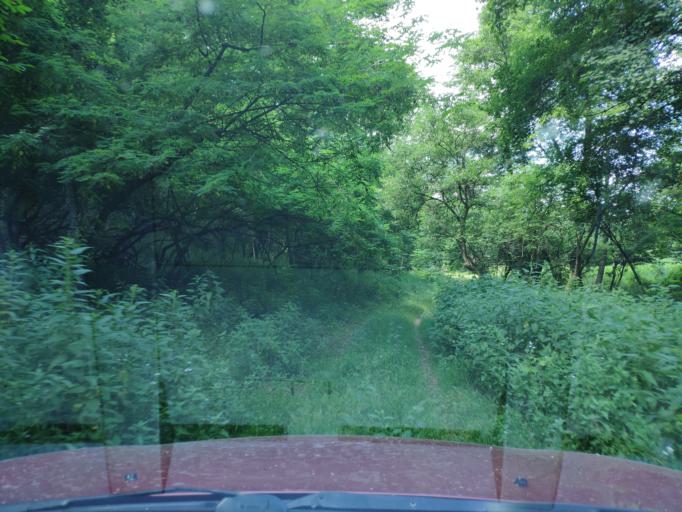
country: HU
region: Borsod-Abauj-Zemplen
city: Arlo
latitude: 48.2573
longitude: 20.1691
